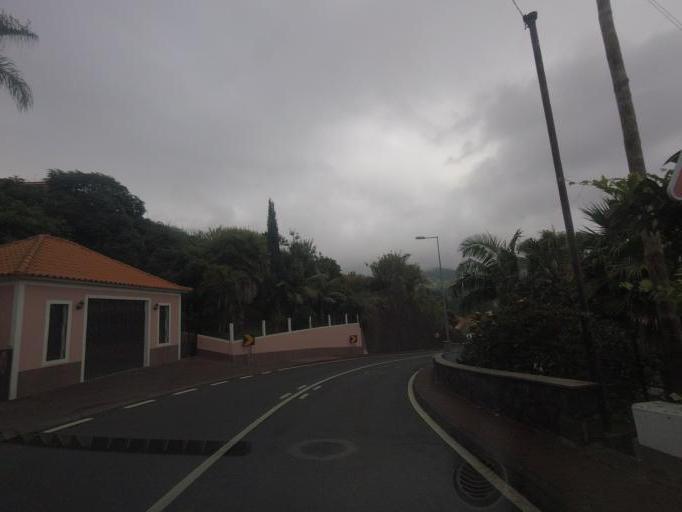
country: PT
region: Madeira
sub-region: Santana
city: Santana
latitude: 32.8216
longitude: -16.8897
